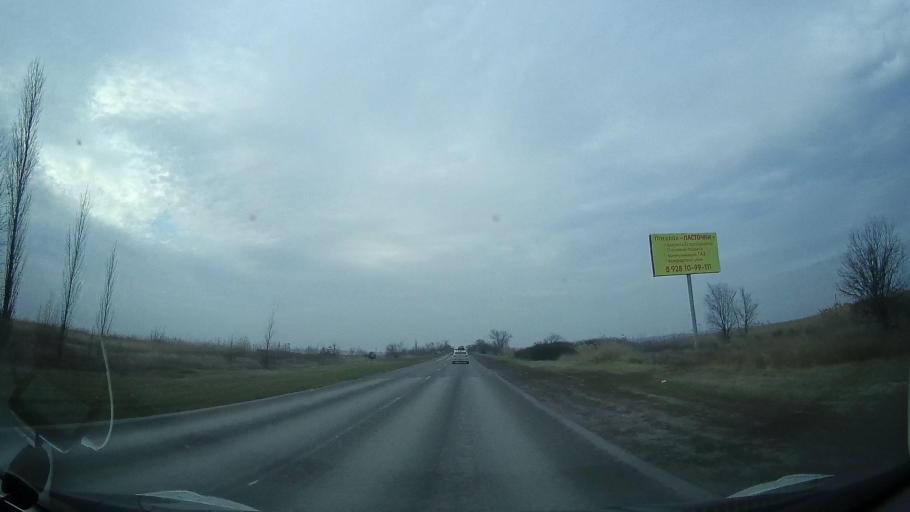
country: RU
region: Rostov
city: Ol'ginskaya
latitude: 47.2032
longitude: 39.9296
